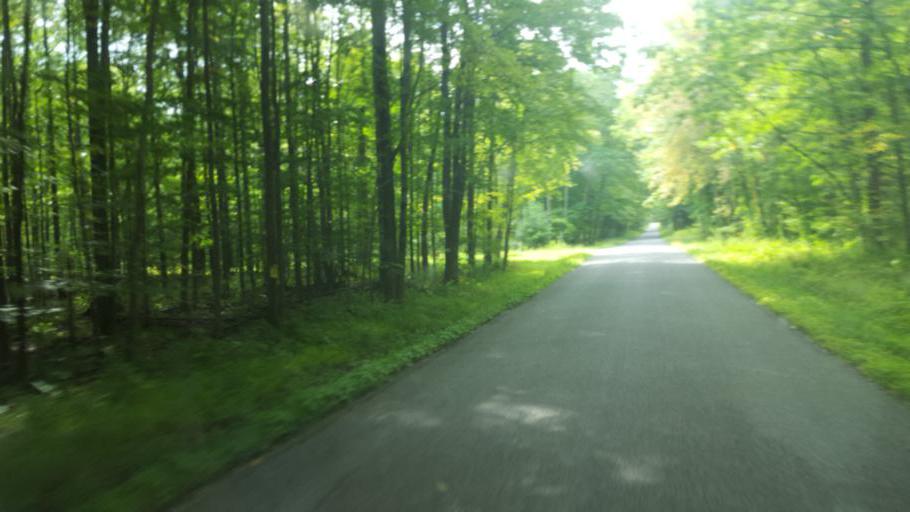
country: US
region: Pennsylvania
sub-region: Crawford County
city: Pymatuning Central
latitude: 41.5273
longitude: -80.4164
